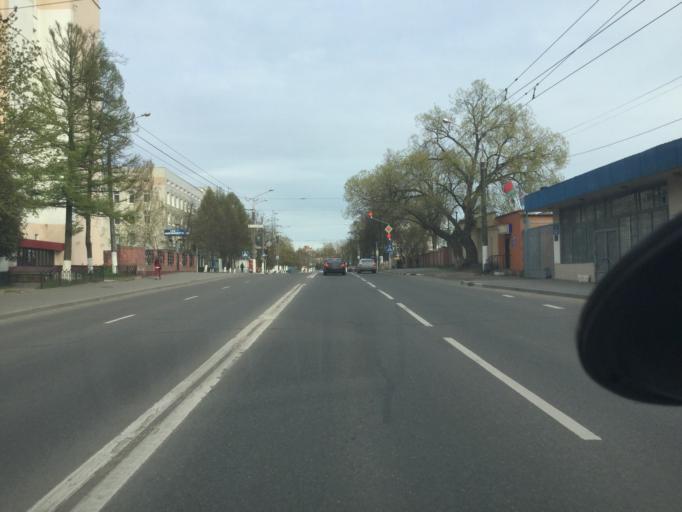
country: BY
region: Vitebsk
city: Vitebsk
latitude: 55.1879
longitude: 30.2150
